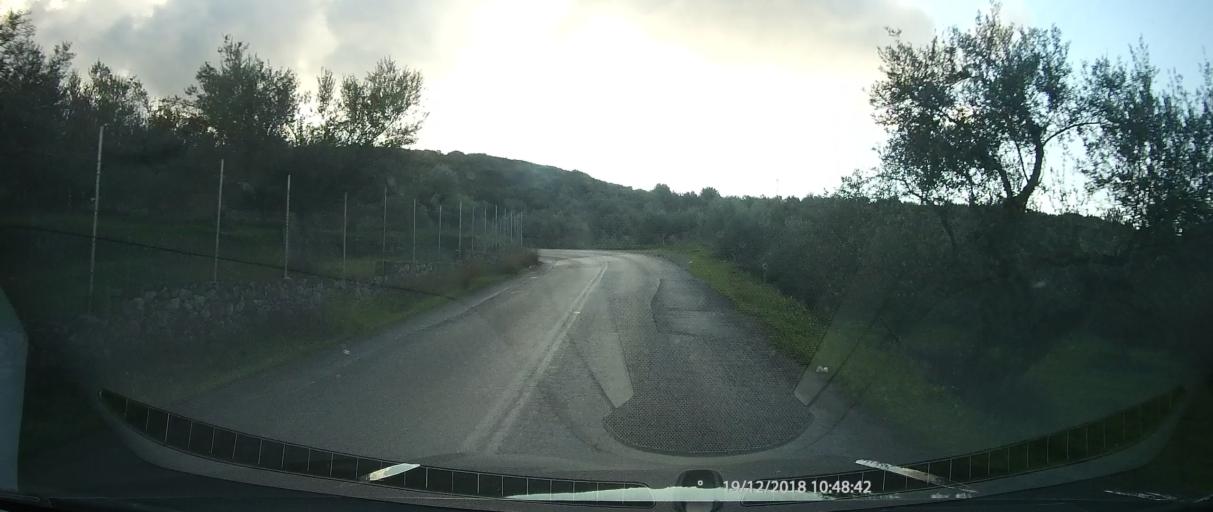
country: GR
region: Peloponnese
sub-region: Nomos Messinias
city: Kardamyli
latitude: 36.9287
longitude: 22.1905
